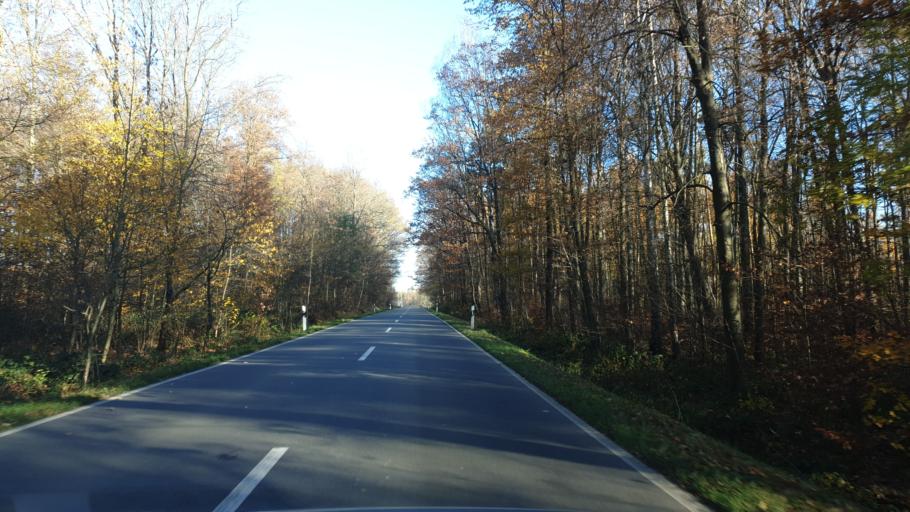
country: DE
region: Saxony-Anhalt
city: Wetterzeube
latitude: 51.0218
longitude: 12.0060
